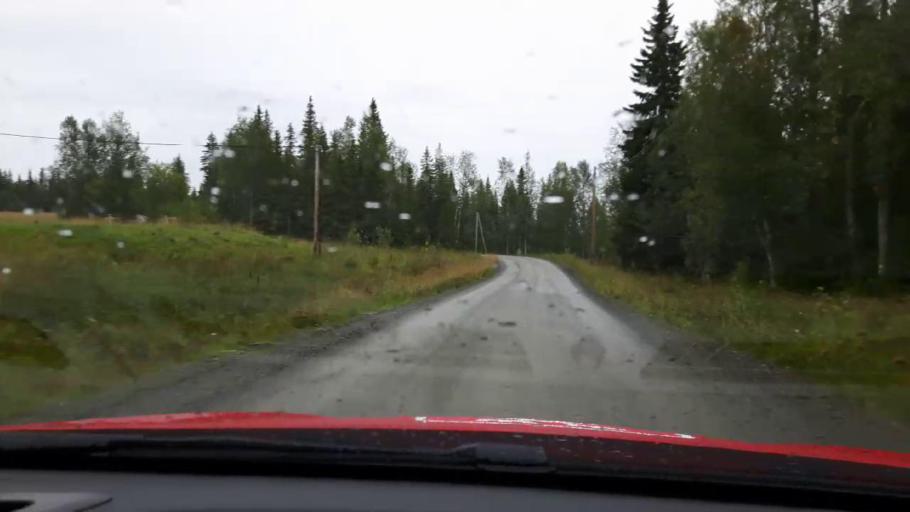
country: SE
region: Jaemtland
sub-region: Are Kommun
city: Are
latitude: 63.5086
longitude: 12.7263
